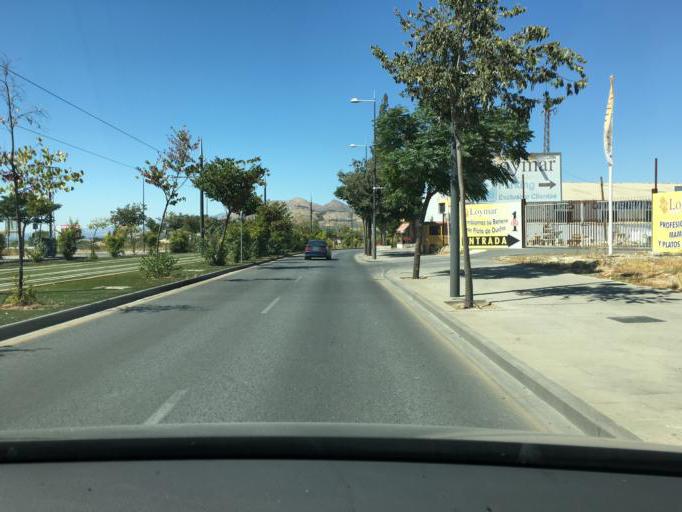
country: ES
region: Andalusia
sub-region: Provincia de Granada
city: Maracena
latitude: 37.2159
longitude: -3.6389
